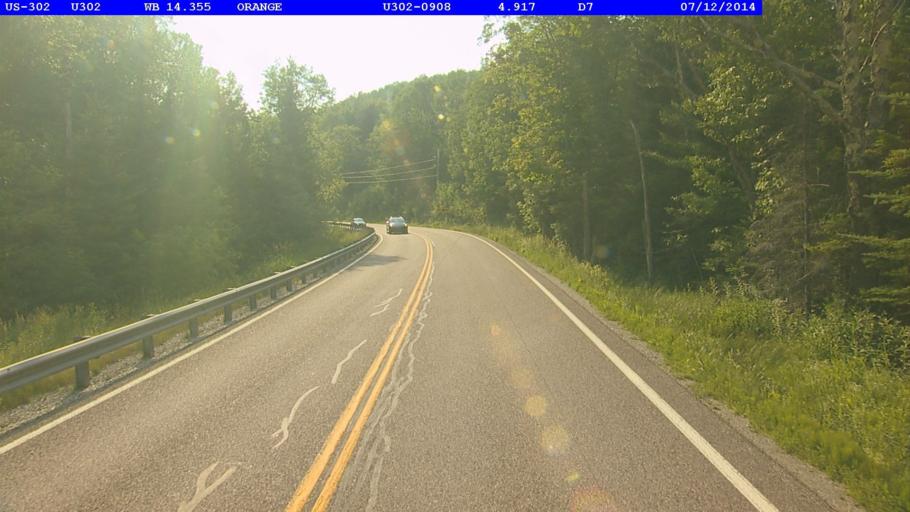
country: US
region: Vermont
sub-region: Washington County
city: South Barre
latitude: 44.1430
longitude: -72.3427
